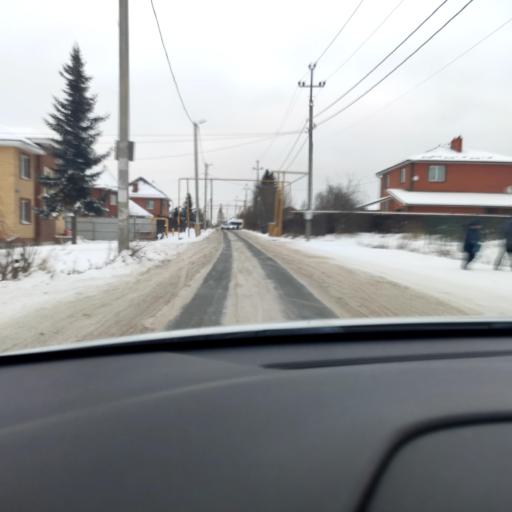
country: RU
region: Tatarstan
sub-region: Gorod Kazan'
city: Kazan
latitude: 55.8756
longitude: 49.1496
